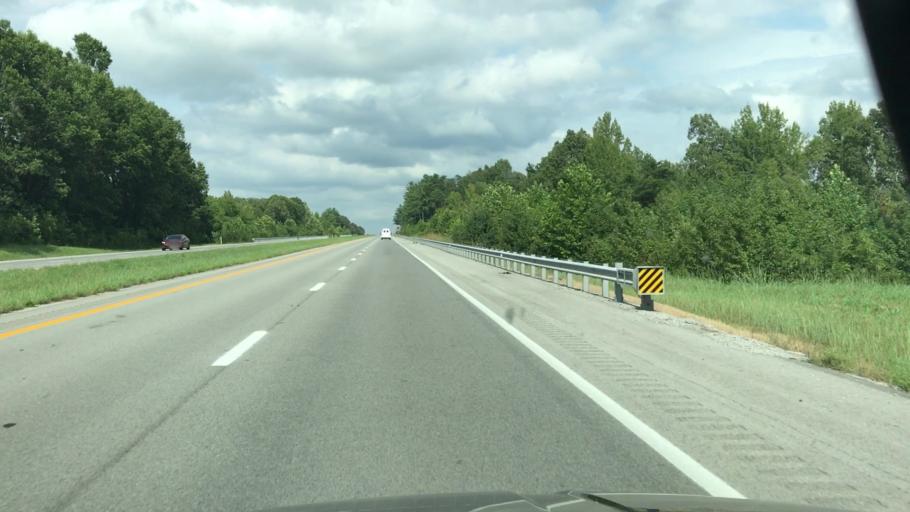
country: US
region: Kentucky
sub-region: Hopkins County
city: Dawson Springs
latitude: 37.1842
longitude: -87.7209
